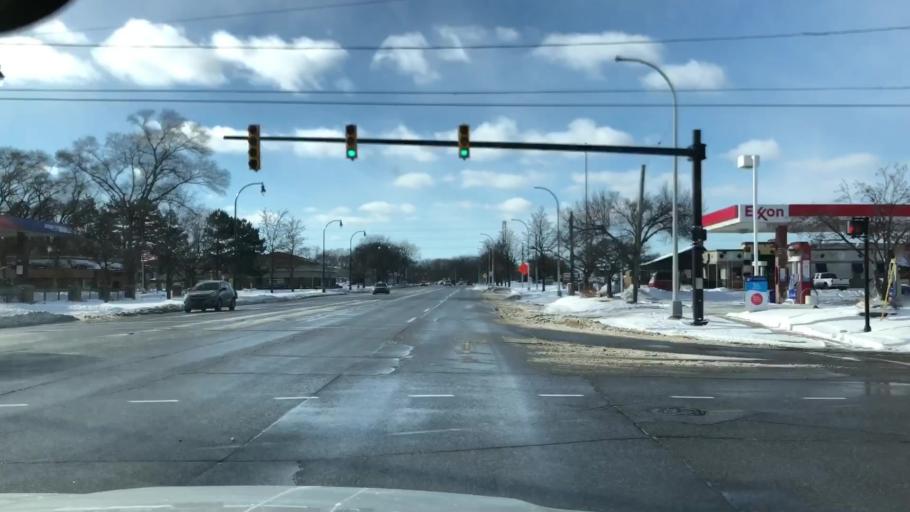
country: US
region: Michigan
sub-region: Wayne County
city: Westland
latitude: 42.3678
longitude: -83.4014
